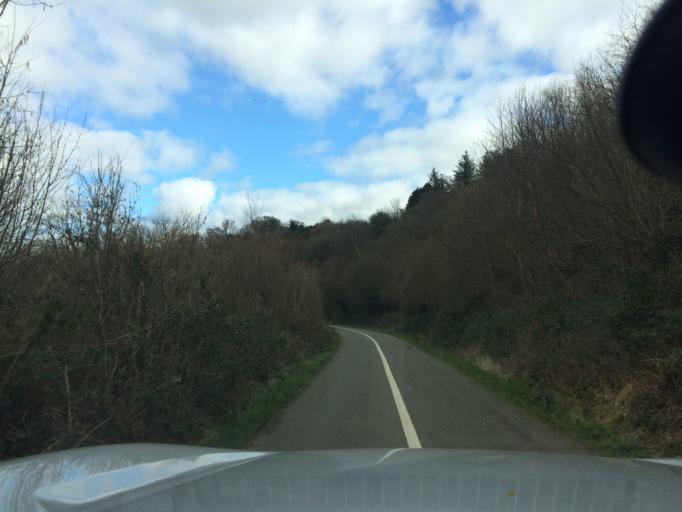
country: IE
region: Munster
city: Carrick-on-Suir
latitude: 52.2785
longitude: -7.4303
